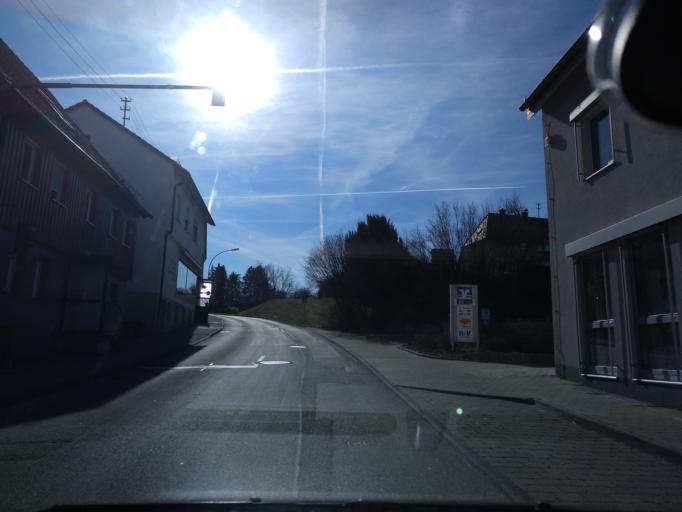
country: DE
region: Baden-Wuerttemberg
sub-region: Regierungsbezirk Stuttgart
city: Mainhardt
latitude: 49.0797
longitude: 9.5572
